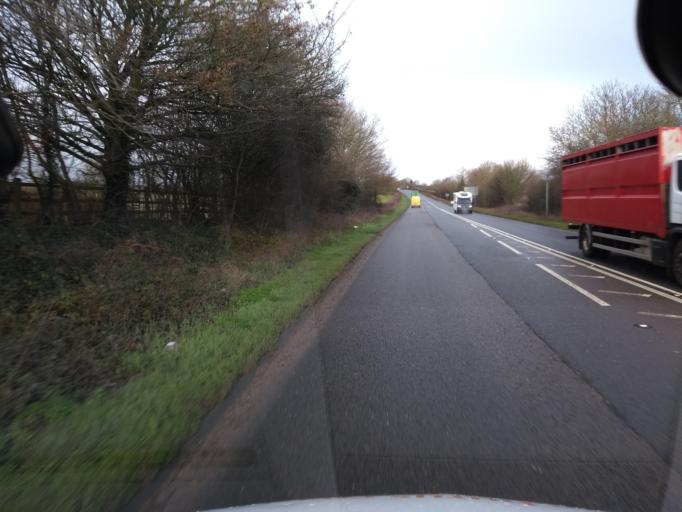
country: GB
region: England
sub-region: Somerset
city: Creech Saint Michael
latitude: 50.9942
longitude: -3.0161
